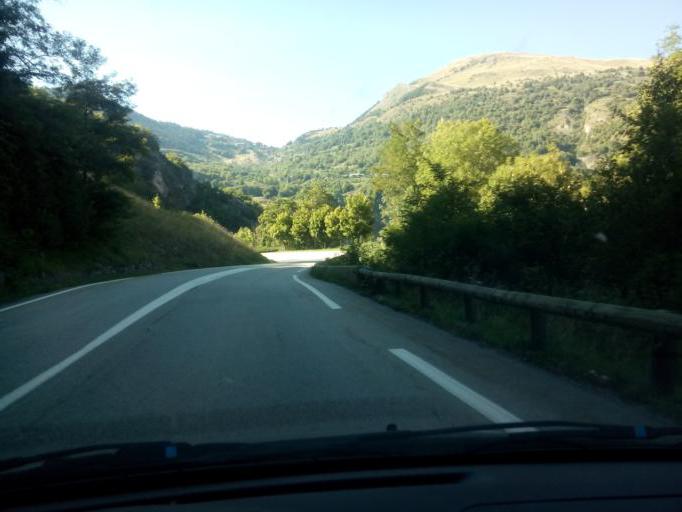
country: FR
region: Rhone-Alpes
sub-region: Departement de l'Isere
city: Mont-de-Lans
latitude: 45.0379
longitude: 6.1033
